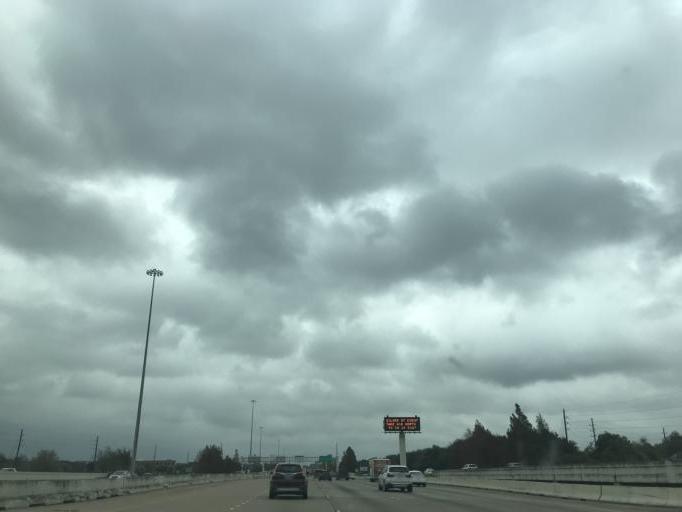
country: US
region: Texas
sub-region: Fort Bend County
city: Sugar Land
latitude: 29.6012
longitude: -95.6195
